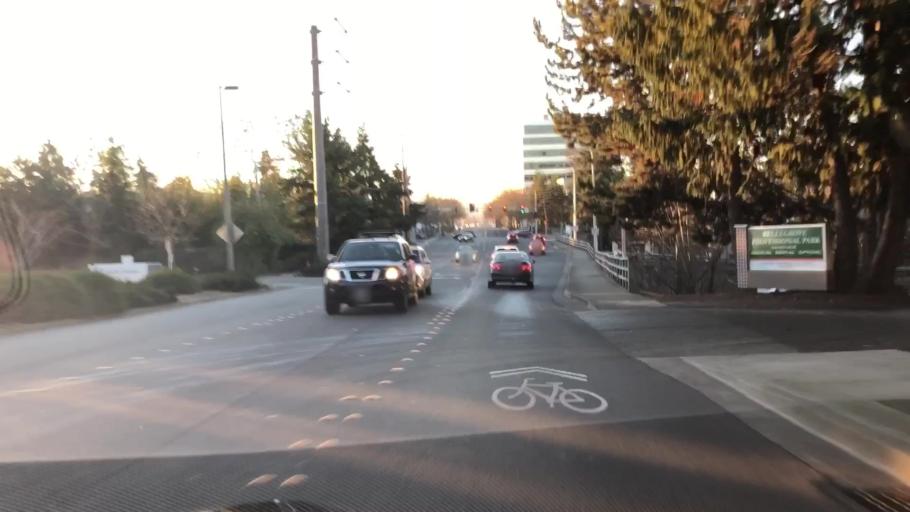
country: US
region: Washington
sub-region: King County
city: Bellevue
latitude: 47.6243
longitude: -122.1857
